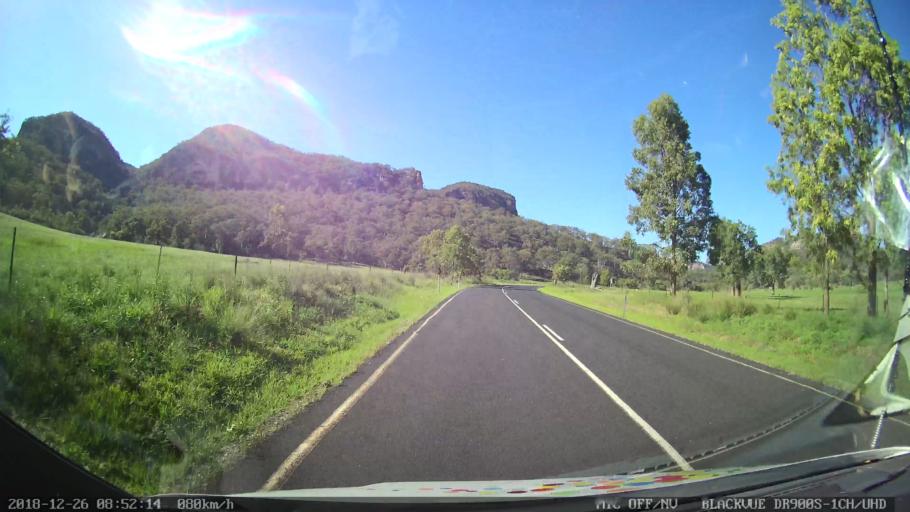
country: AU
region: New South Wales
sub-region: Mid-Western Regional
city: Kandos
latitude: -32.5945
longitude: 150.0870
